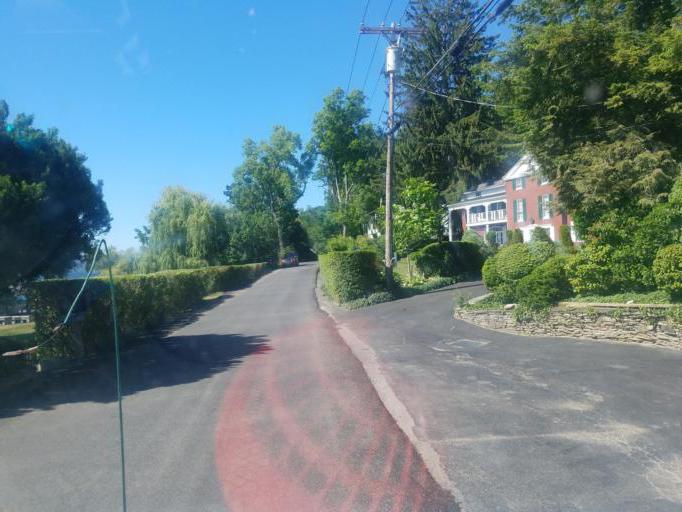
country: US
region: New York
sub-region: Ontario County
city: Naples
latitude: 42.7281
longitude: -77.3525
